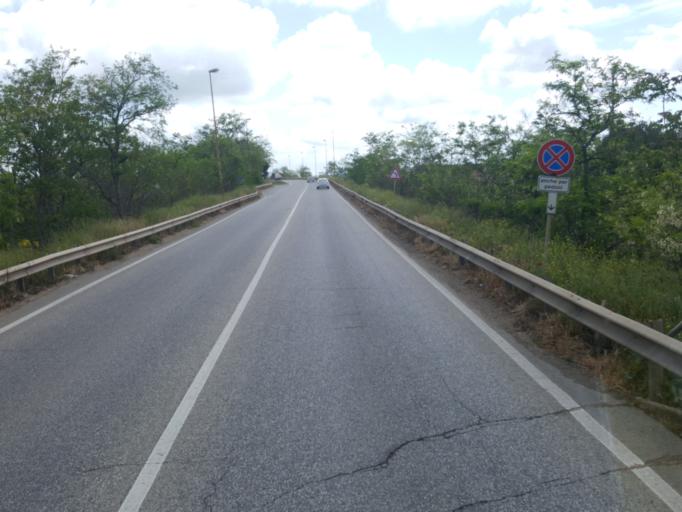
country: IT
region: Apulia
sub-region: Provincia di Bari
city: Altamura
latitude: 40.8153
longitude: 16.5538
